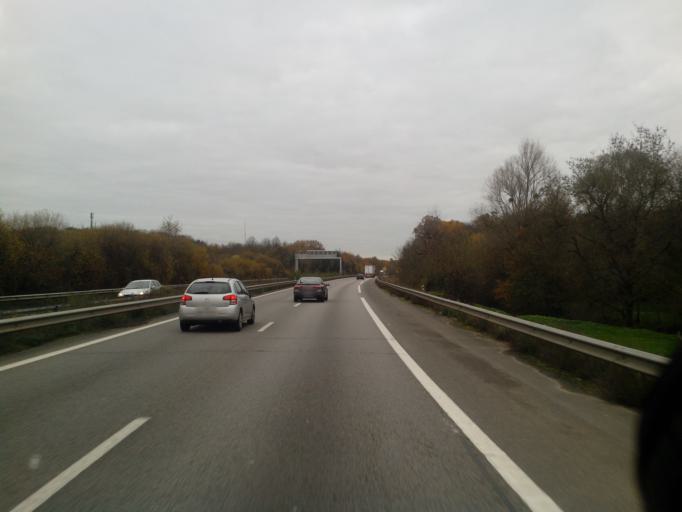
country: FR
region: Pays de la Loire
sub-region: Departement de la Loire-Atlantique
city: Basse-Goulaine
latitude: 47.2135
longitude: -1.4517
